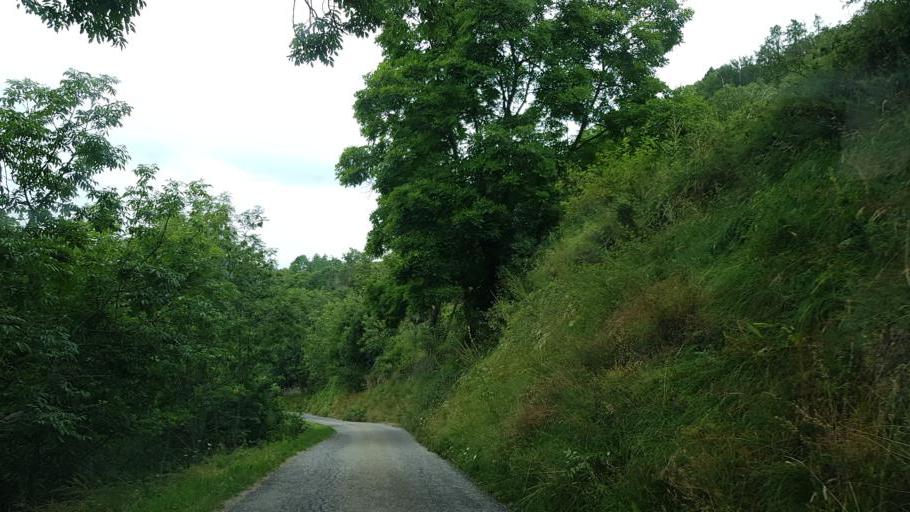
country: IT
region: Piedmont
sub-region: Provincia di Cuneo
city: Stroppo
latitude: 44.5078
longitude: 7.1134
